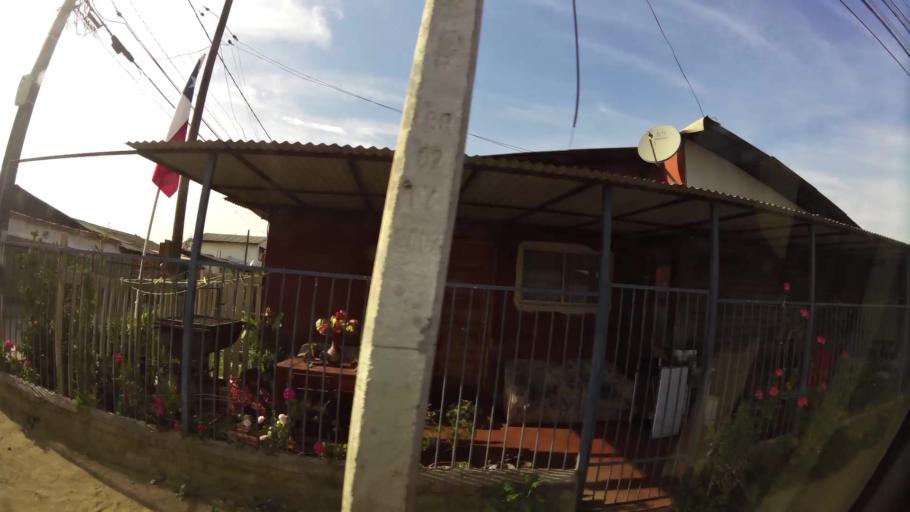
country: CL
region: Santiago Metropolitan
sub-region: Provincia de Talagante
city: Talagante
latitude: -33.6694
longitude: -70.9359
